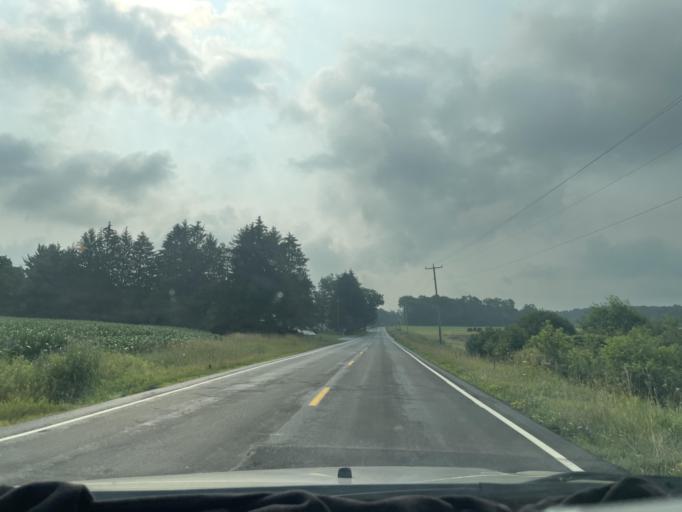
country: US
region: Maryland
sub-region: Garrett County
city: Mountain Lake Park
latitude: 39.2966
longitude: -79.3745
